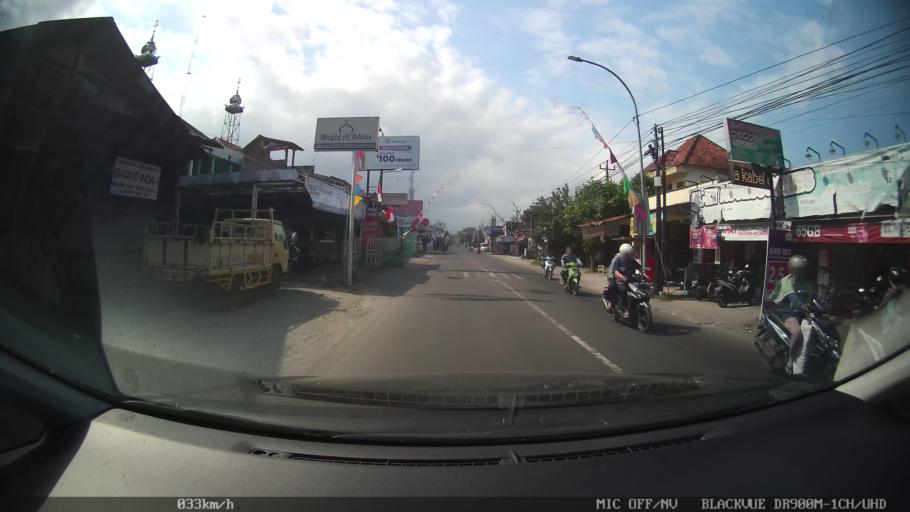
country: ID
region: Daerah Istimewa Yogyakarta
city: Sewon
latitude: -7.8459
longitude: 110.3910
